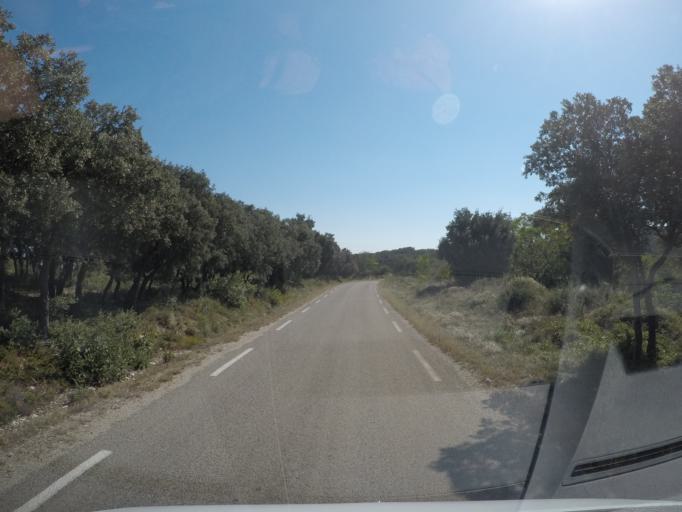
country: FR
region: Languedoc-Roussillon
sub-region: Departement du Gard
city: Tavel
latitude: 44.0138
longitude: 4.6527
